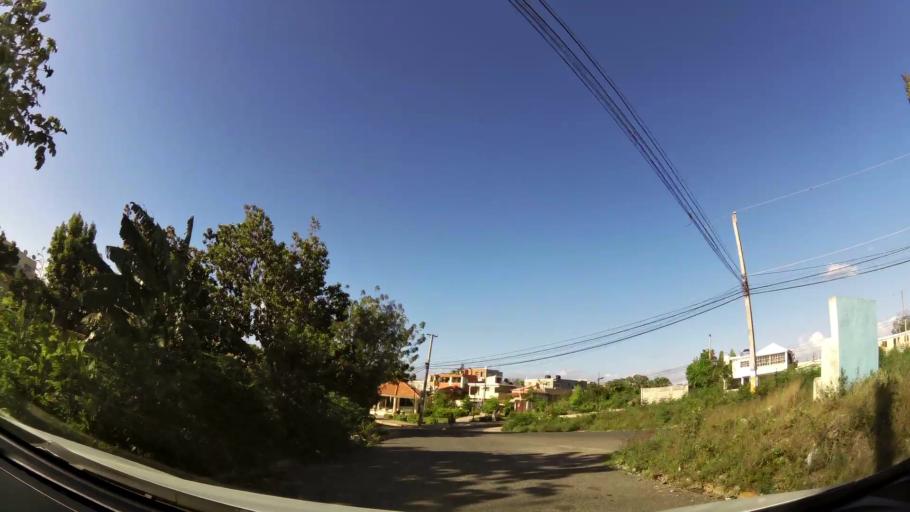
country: DO
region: Santo Domingo
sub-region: Santo Domingo
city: Santo Domingo Este
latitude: 18.4900
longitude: -69.8062
